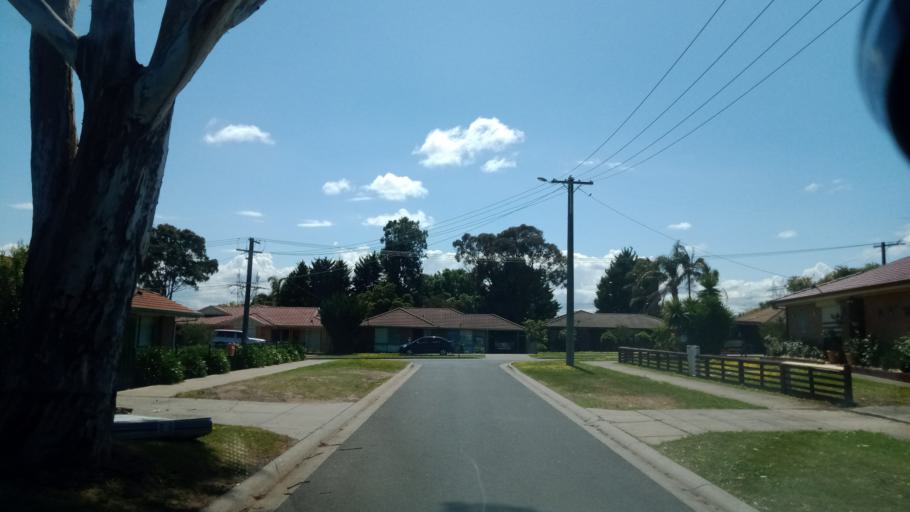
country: AU
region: Victoria
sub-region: Casey
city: Cranbourne West
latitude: -38.0916
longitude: 145.2698
